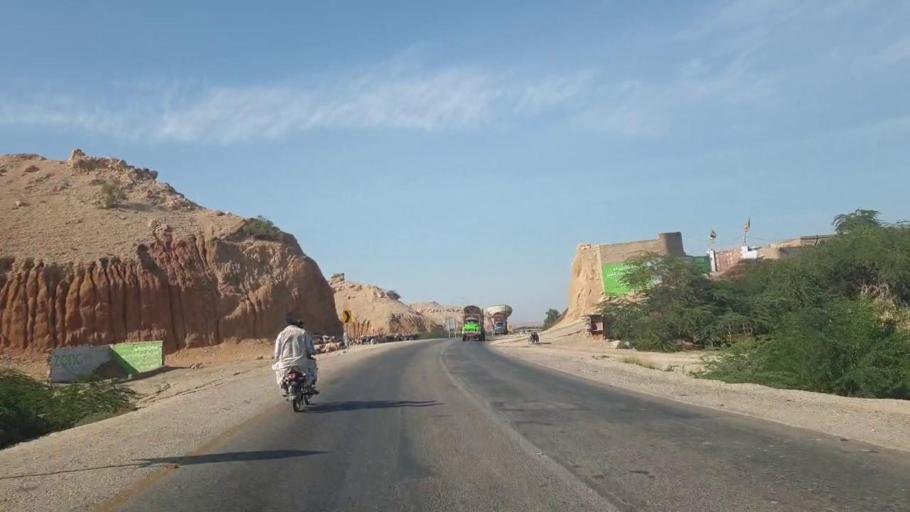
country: PK
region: Sindh
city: Sehwan
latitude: 26.3159
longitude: 67.8898
